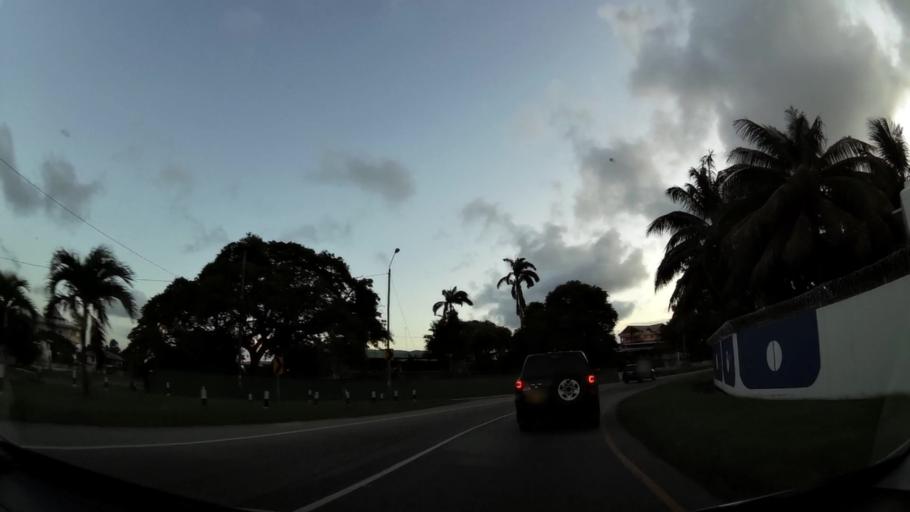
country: GY
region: Demerara-Mahaica
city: Georgetown
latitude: 6.8240
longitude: -58.1374
